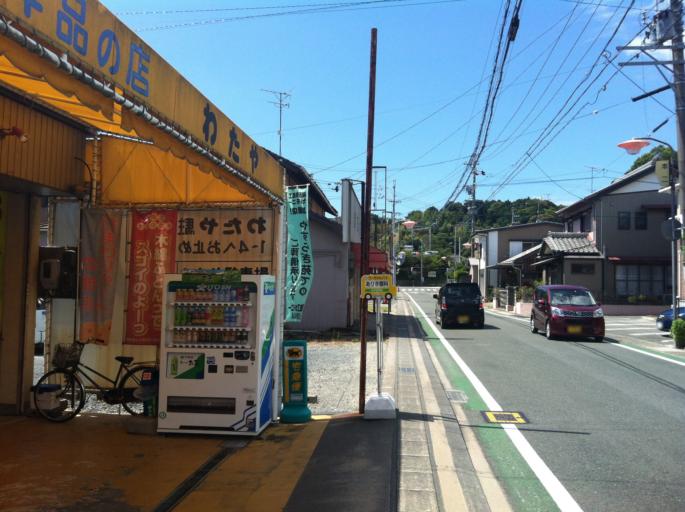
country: JP
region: Shizuoka
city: Kosai-shi
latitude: 34.7155
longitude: 137.5416
